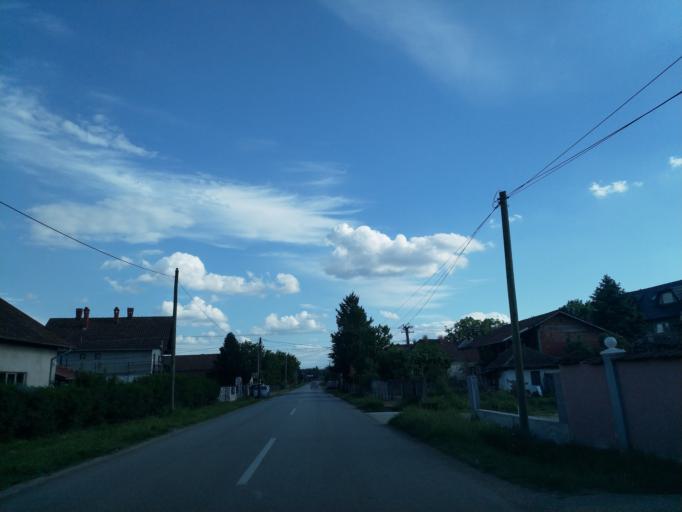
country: RS
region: Central Serbia
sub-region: Sumadijski Okrug
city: Lapovo
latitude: 44.1830
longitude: 21.0916
